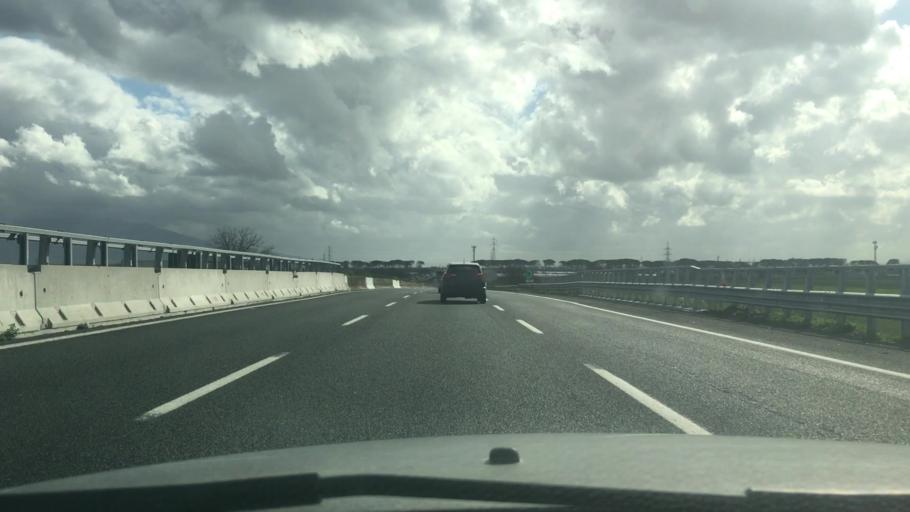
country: IT
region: Campania
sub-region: Provincia di Napoli
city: Pascarola
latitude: 40.9988
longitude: 14.3240
